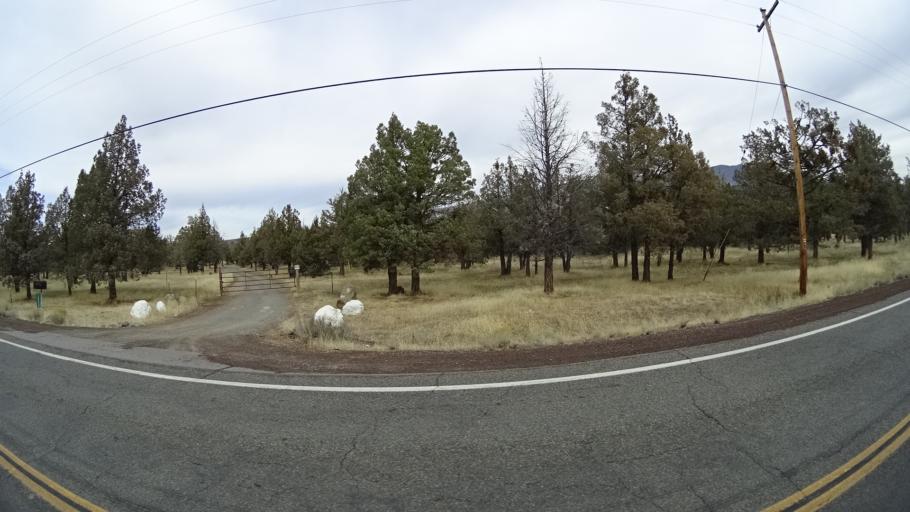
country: US
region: California
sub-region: Siskiyou County
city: Weed
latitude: 41.5925
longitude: -122.3088
